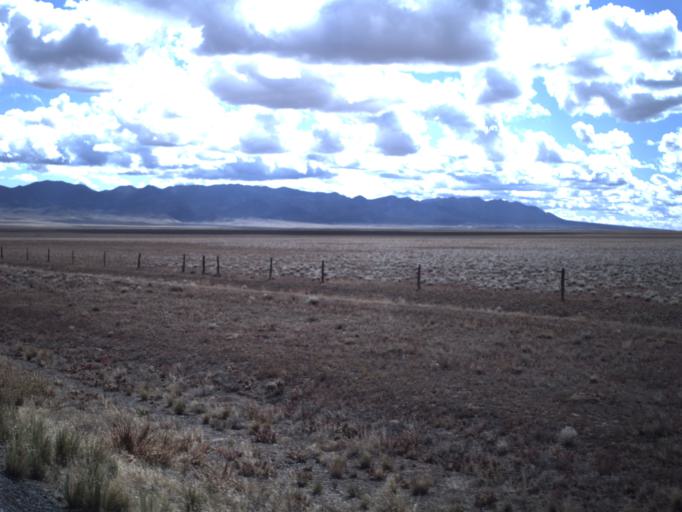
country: US
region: Utah
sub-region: Beaver County
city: Milford
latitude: 38.5529
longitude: -113.7376
